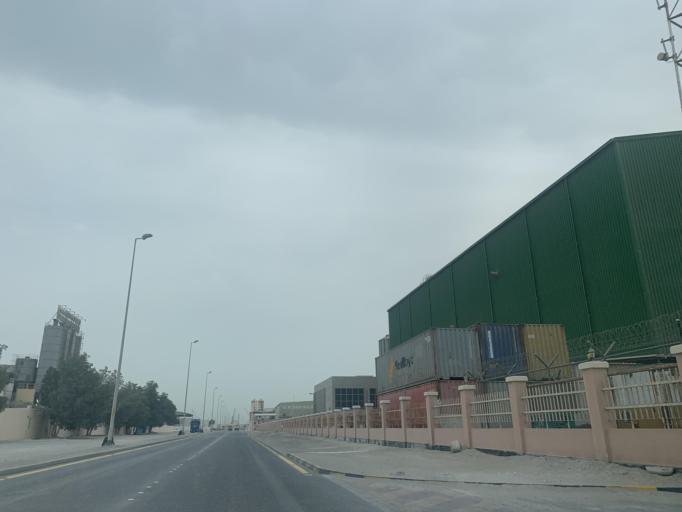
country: BH
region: Muharraq
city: Al Hadd
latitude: 26.2098
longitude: 50.6618
